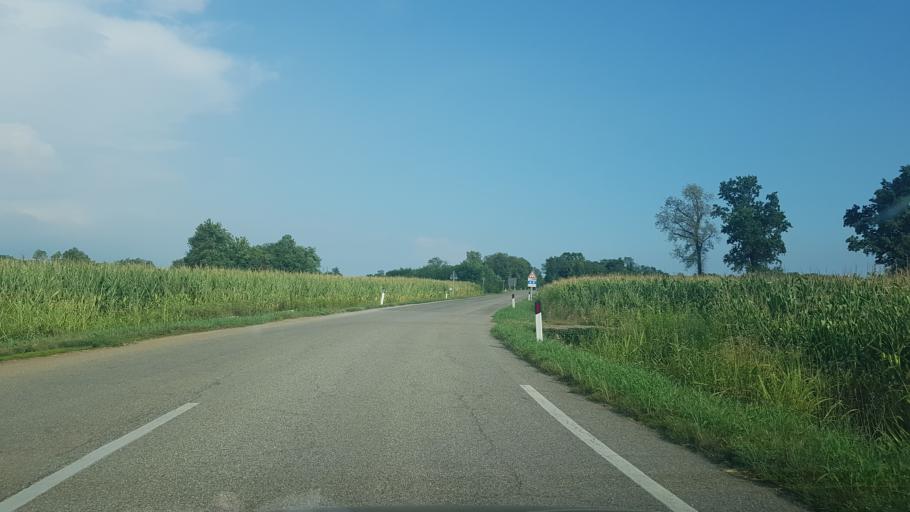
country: IT
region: Friuli Venezia Giulia
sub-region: Provincia di Udine
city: Colloredo di Prato
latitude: 46.0573
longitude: 13.1167
